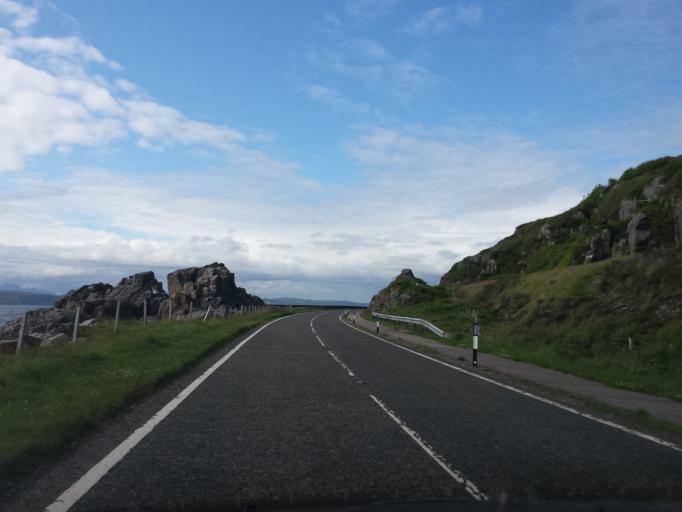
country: GB
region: Scotland
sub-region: Highland
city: Portree
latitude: 56.9987
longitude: -5.8335
